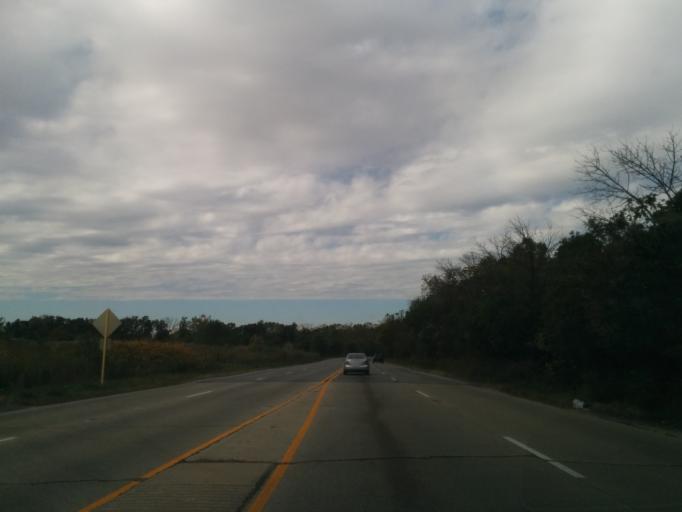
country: US
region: Illinois
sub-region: Cook County
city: River Grove
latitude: 41.9170
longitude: -87.8359
